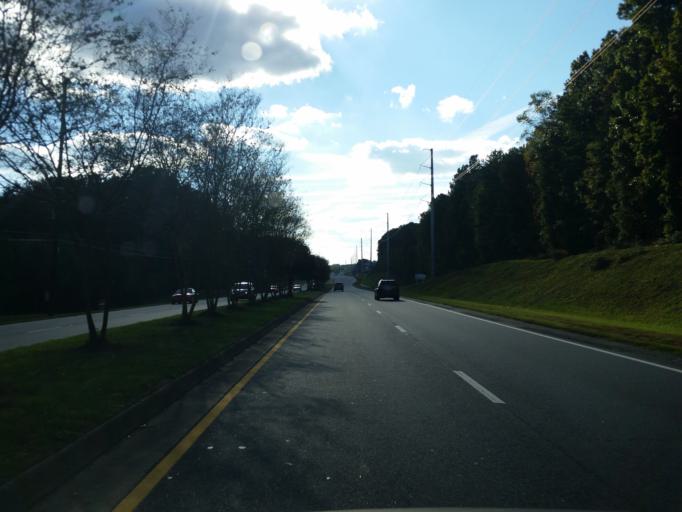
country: US
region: Georgia
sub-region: Paulding County
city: Hiram
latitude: 33.9364
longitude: -84.7181
